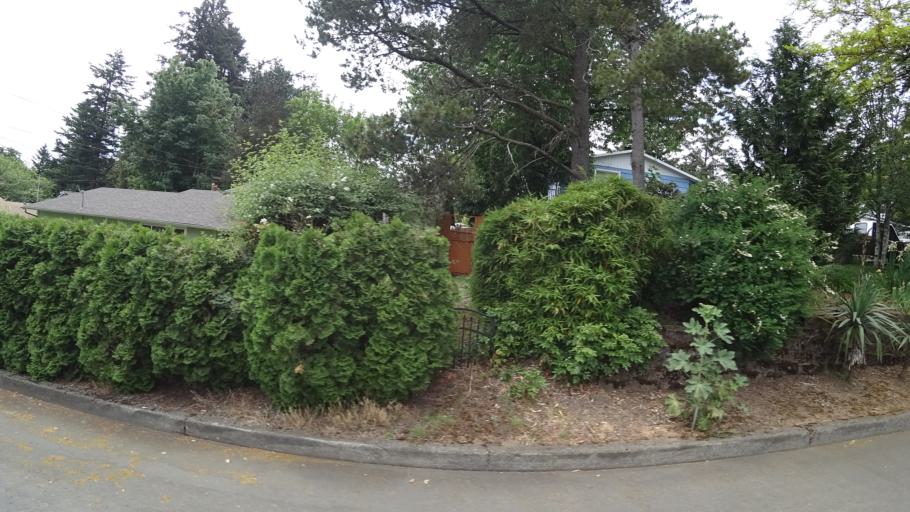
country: US
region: Oregon
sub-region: Multnomah County
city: Lents
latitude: 45.5006
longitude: -122.5193
